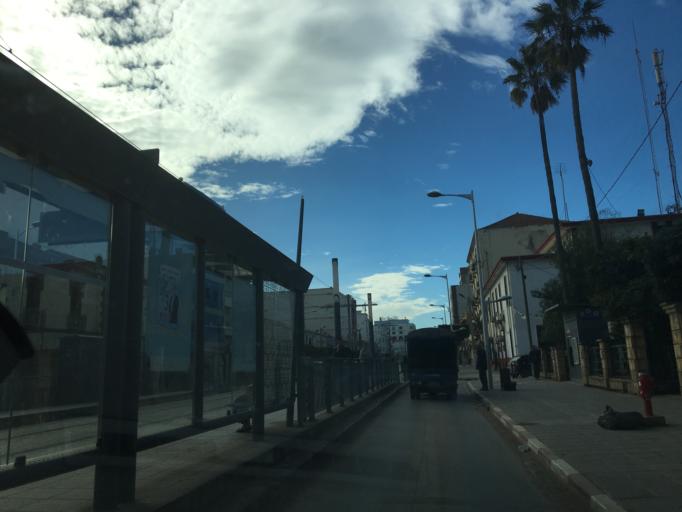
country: DZ
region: Alger
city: Bordj el Kiffan
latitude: 36.7471
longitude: 3.1911
